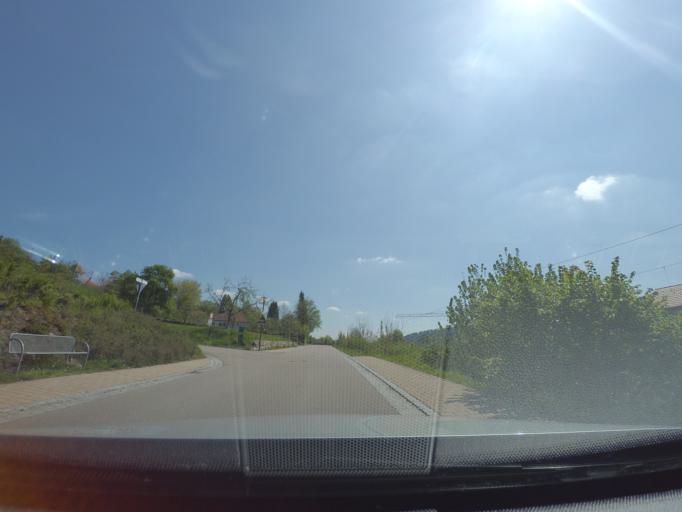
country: DE
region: Baden-Wuerttemberg
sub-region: Regierungsbezirk Stuttgart
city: Fichtenberg
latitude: 48.9871
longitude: 9.7161
